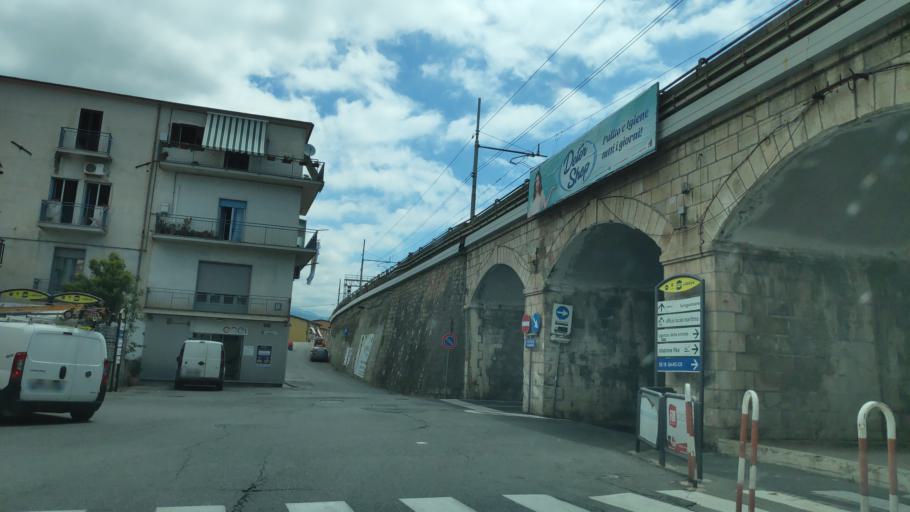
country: IT
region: Calabria
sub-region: Provincia di Cosenza
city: Paola
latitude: 39.3585
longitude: 16.0342
